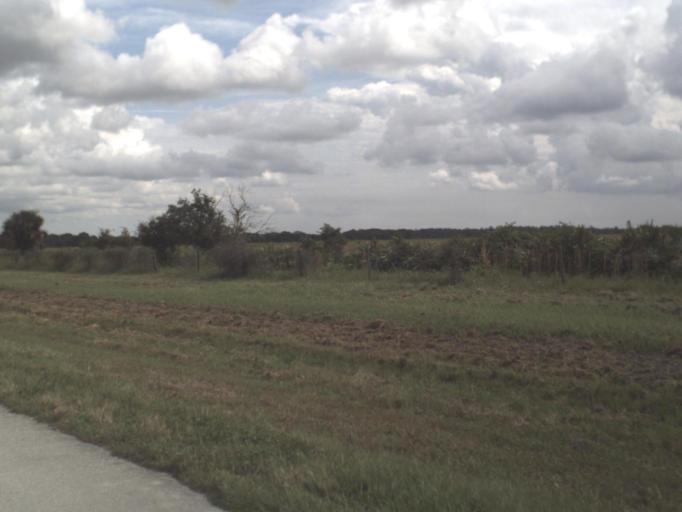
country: US
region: Florida
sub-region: Hendry County
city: Port LaBelle
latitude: 26.8309
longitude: -81.3969
